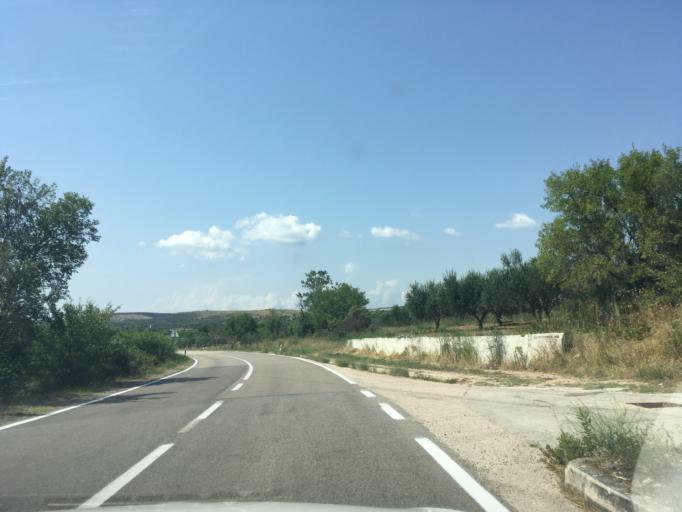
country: HR
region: Zadarska
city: Benkovac
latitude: 43.9778
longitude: 15.7042
